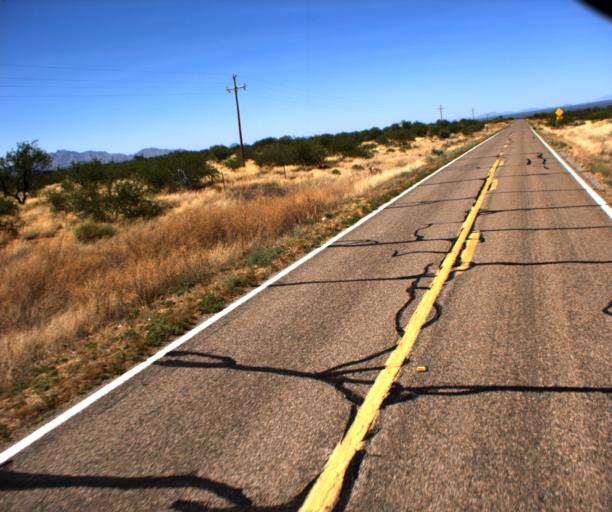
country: US
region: Arizona
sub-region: Pima County
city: Three Points
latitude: 31.7558
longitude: -111.4782
